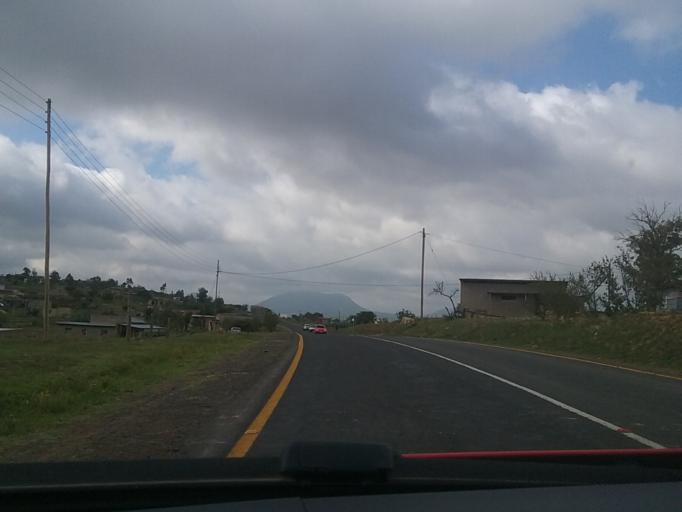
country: LS
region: Berea
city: Teyateyaneng
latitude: -29.1675
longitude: 27.7774
